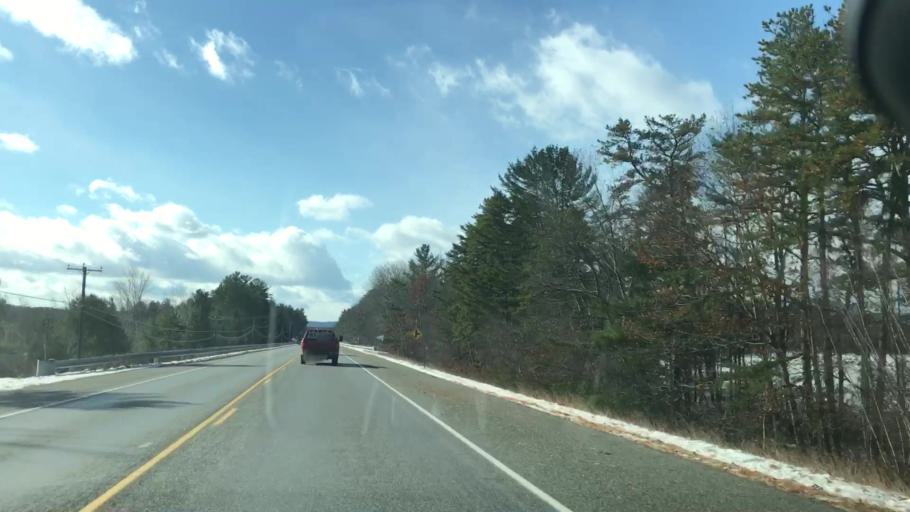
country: US
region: New Hampshire
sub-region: Carroll County
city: Freedom
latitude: 43.7805
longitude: -71.1037
